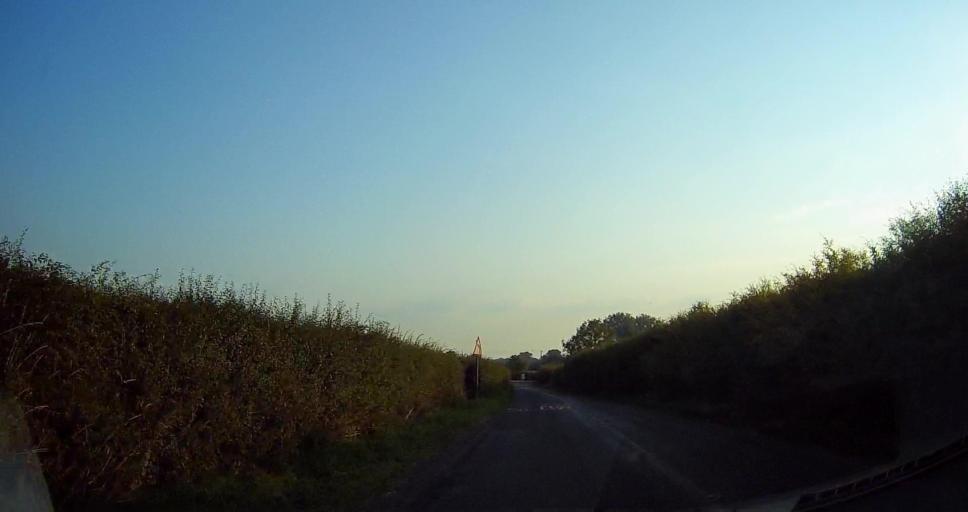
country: GB
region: England
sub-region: Cheshire East
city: Nantwich
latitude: 53.0467
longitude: -2.5205
